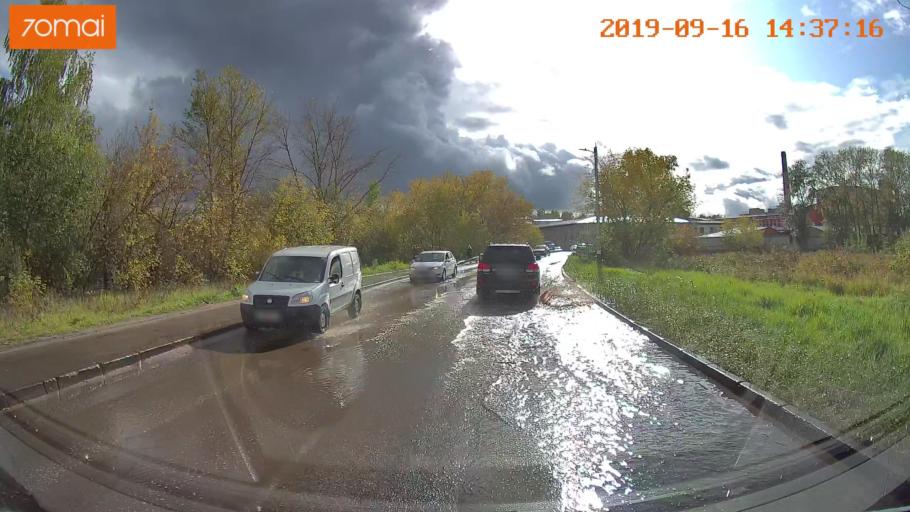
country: RU
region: Ivanovo
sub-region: Gorod Ivanovo
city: Ivanovo
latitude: 57.0141
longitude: 40.9549
